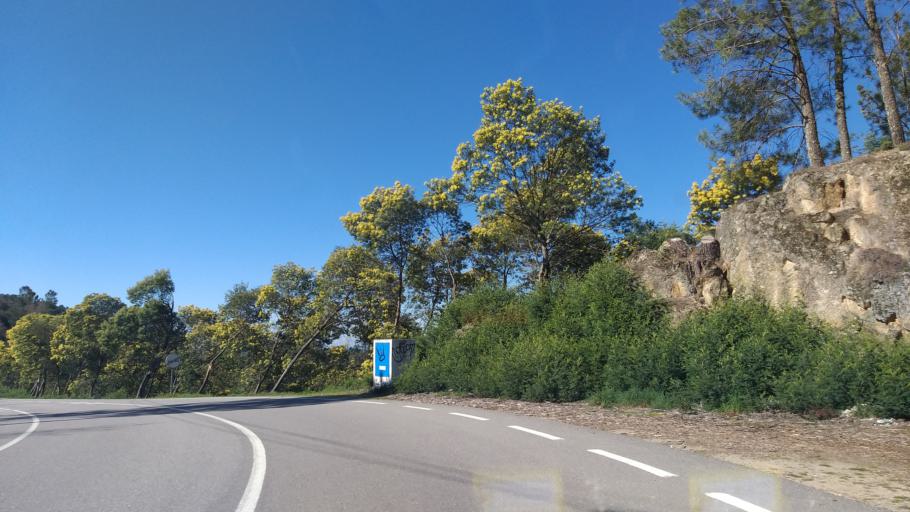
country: PT
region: Guarda
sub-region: Manteigas
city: Manteigas
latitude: 40.5066
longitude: -7.5706
